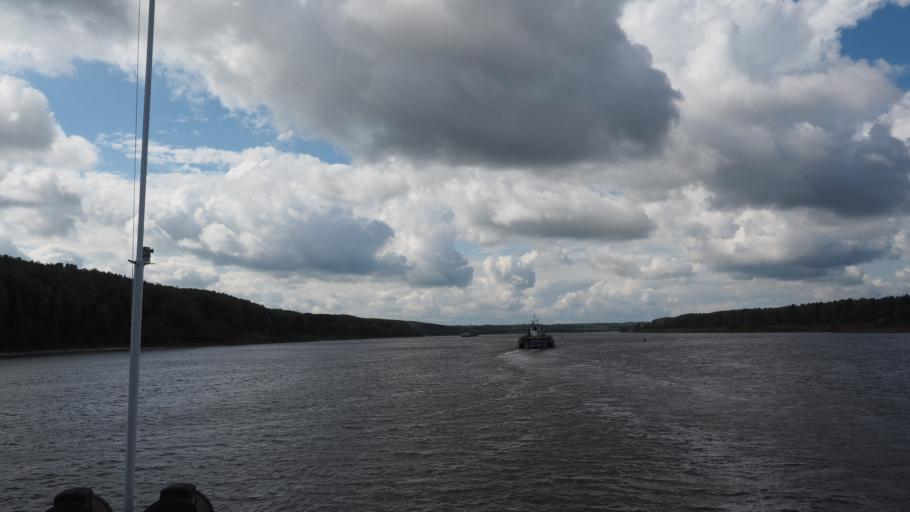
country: RU
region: Jaroslavl
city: Tutayev
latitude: 57.9284
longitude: 39.4185
